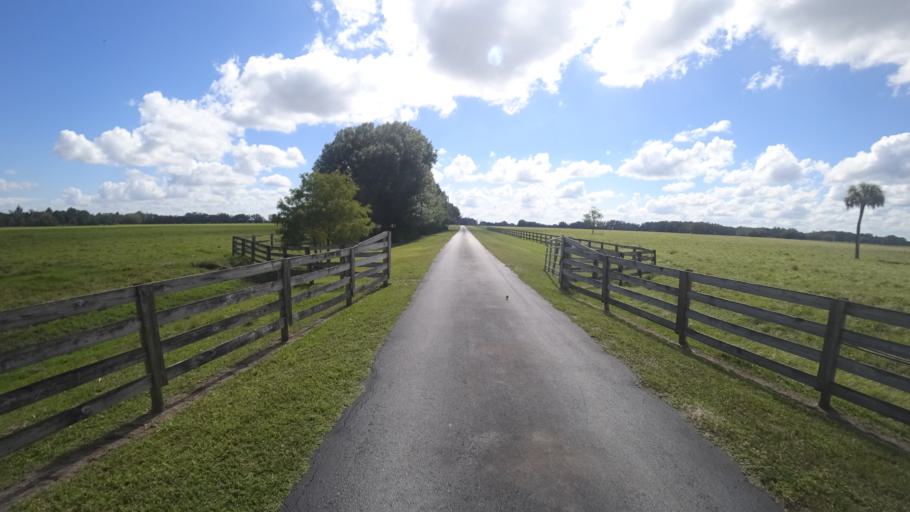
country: US
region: Florida
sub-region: Sarasota County
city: Lake Sarasota
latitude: 27.3388
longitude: -82.1545
